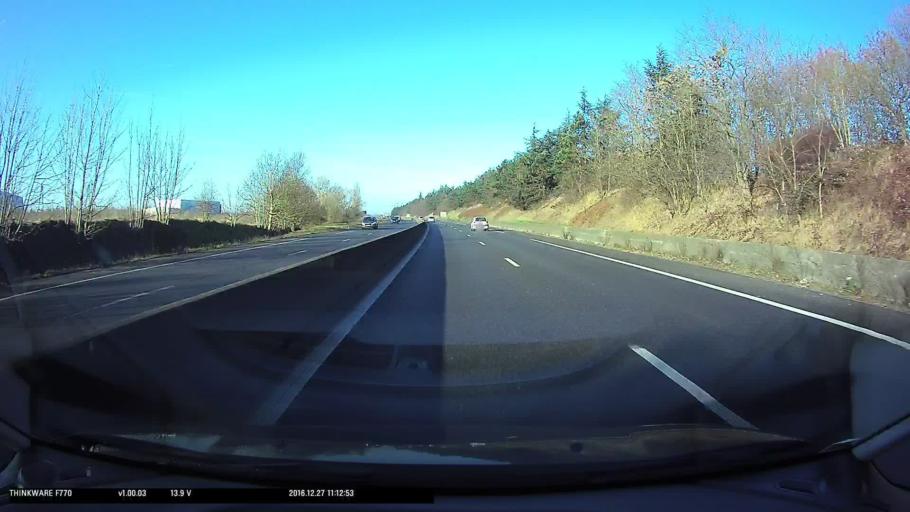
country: FR
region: Ile-de-France
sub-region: Departement du Val-d'Oise
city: Osny
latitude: 49.0536
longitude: 2.0604
